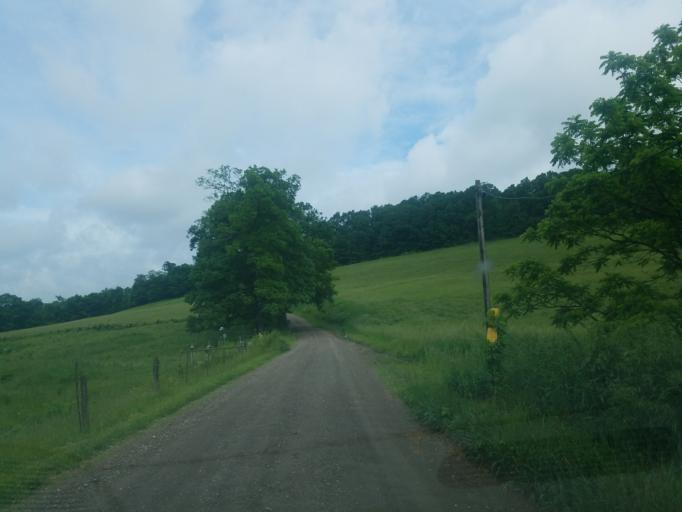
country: US
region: Ohio
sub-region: Holmes County
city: Millersburg
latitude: 40.4777
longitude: -81.8088
